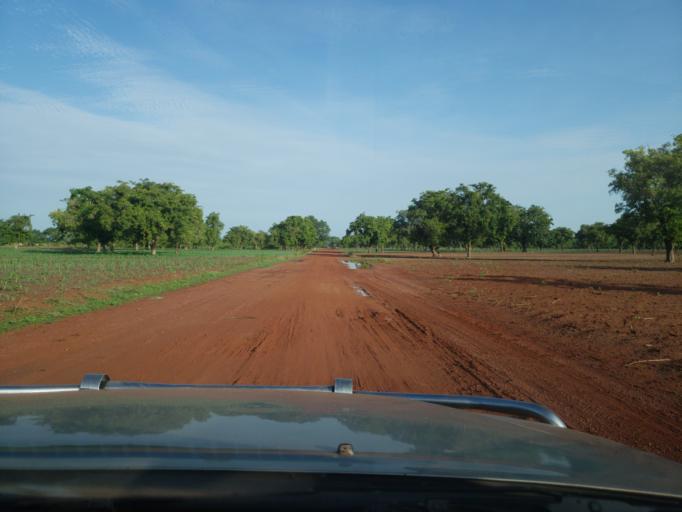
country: ML
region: Sikasso
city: Koutiala
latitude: 12.4236
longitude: -5.5903
